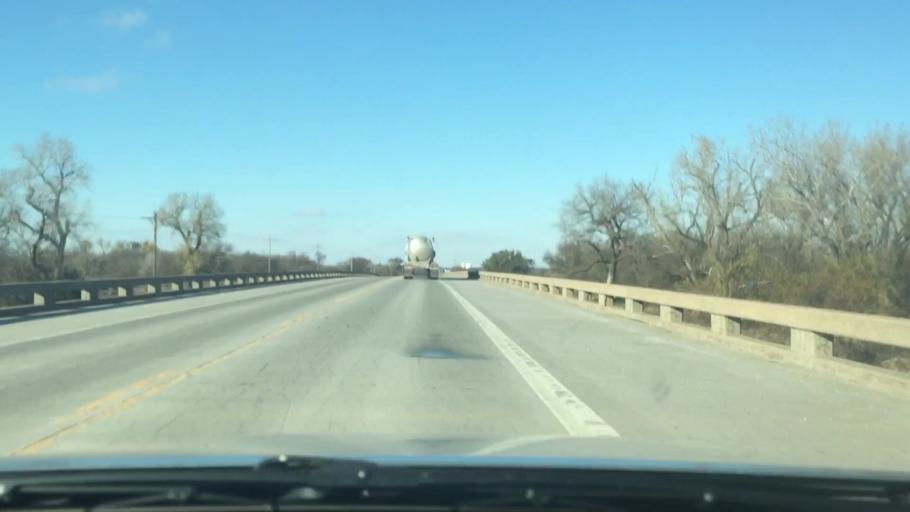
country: US
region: Kansas
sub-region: Rice County
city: Sterling
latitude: 38.1694
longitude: -98.2068
